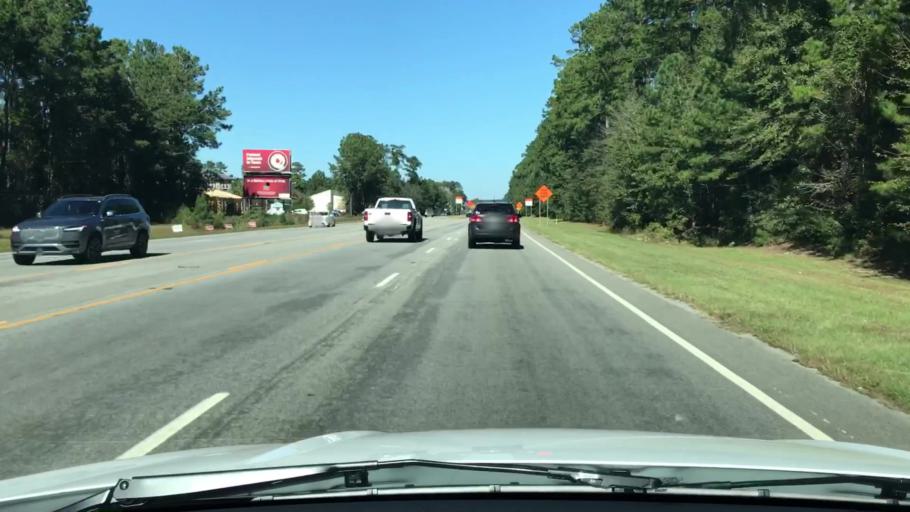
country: US
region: South Carolina
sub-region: Beaufort County
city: Bluffton
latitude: 32.3065
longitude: -80.9350
